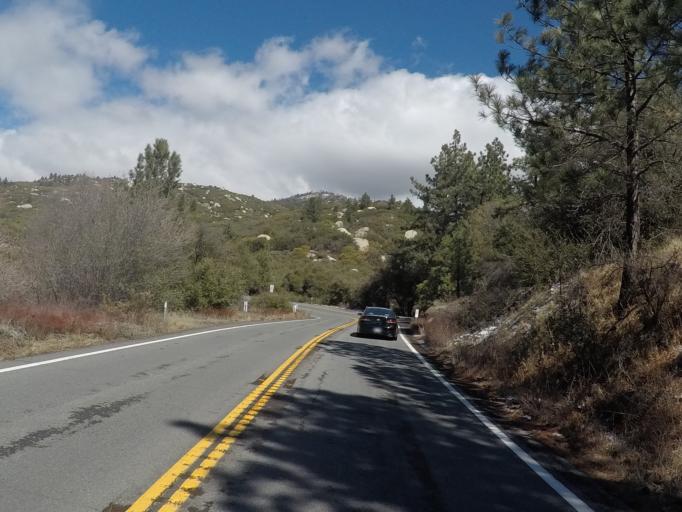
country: US
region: California
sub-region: Riverside County
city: Idyllwild
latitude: 33.7115
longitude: -116.7171
